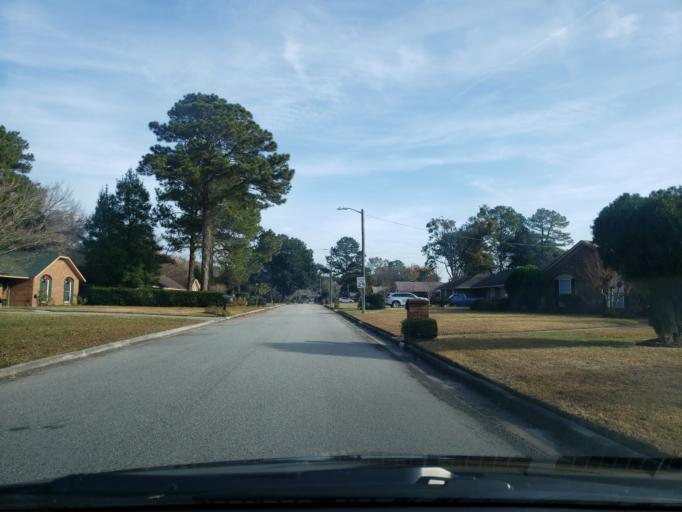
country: US
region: Georgia
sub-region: Chatham County
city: Montgomery
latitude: 31.9983
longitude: -81.1445
